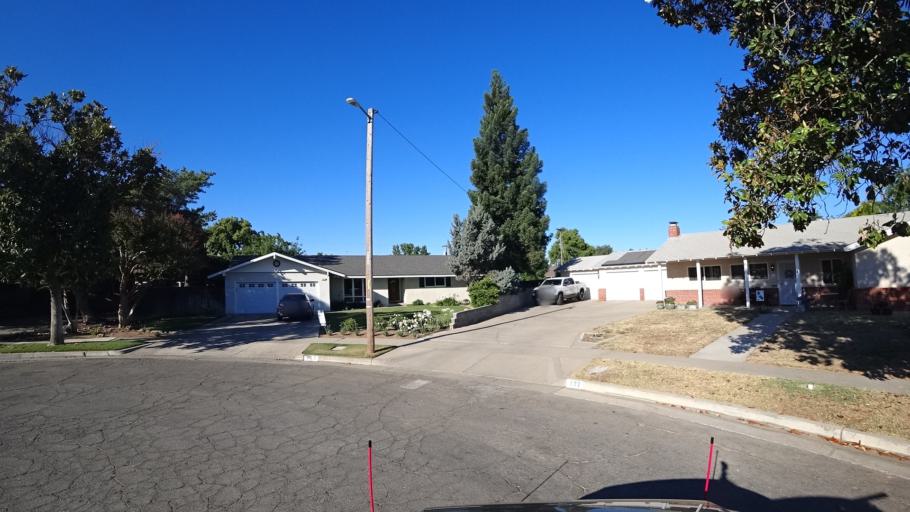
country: US
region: California
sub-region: Fresno County
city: Fresno
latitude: 36.8020
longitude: -119.8210
